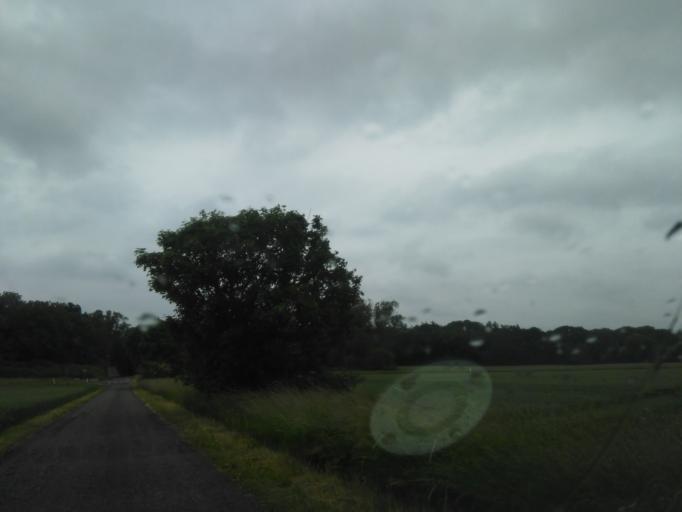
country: DK
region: Capital Region
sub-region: Bornholm Kommune
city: Akirkeby
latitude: 55.0459
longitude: 14.8336
